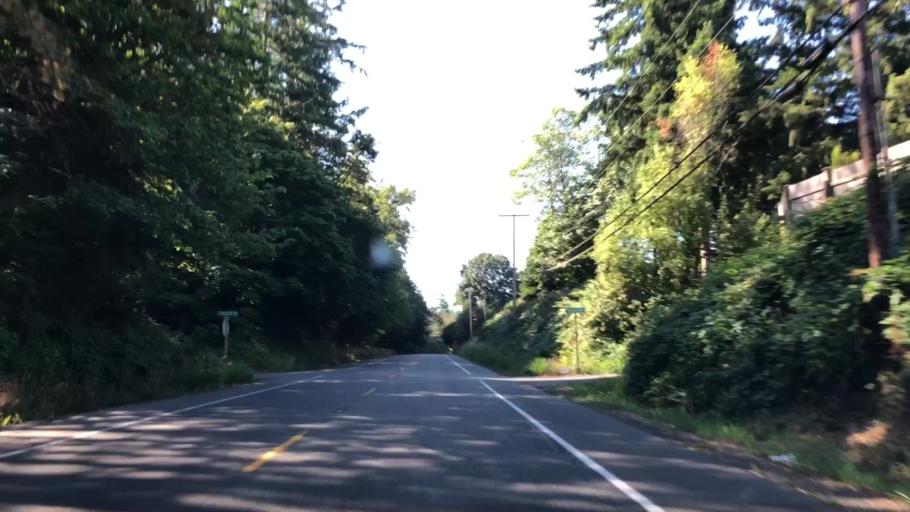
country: US
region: Washington
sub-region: Kitsap County
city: Kingston
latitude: 47.7828
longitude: -122.5013
